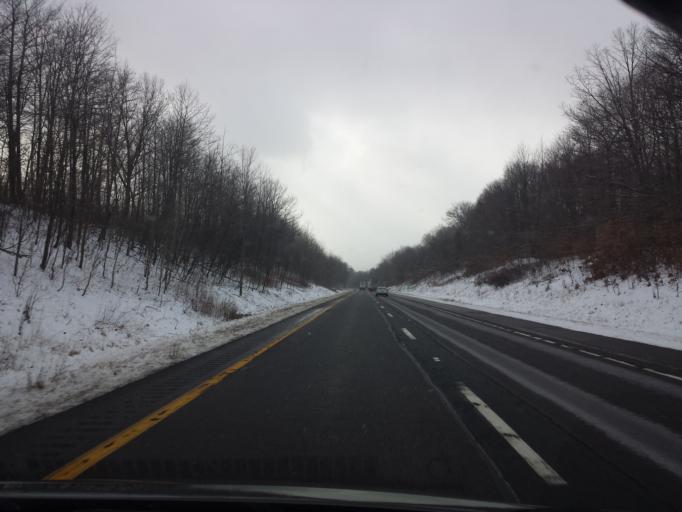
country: US
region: Pennsylvania
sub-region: Luzerne County
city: White Haven
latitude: 41.0765
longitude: -75.6735
